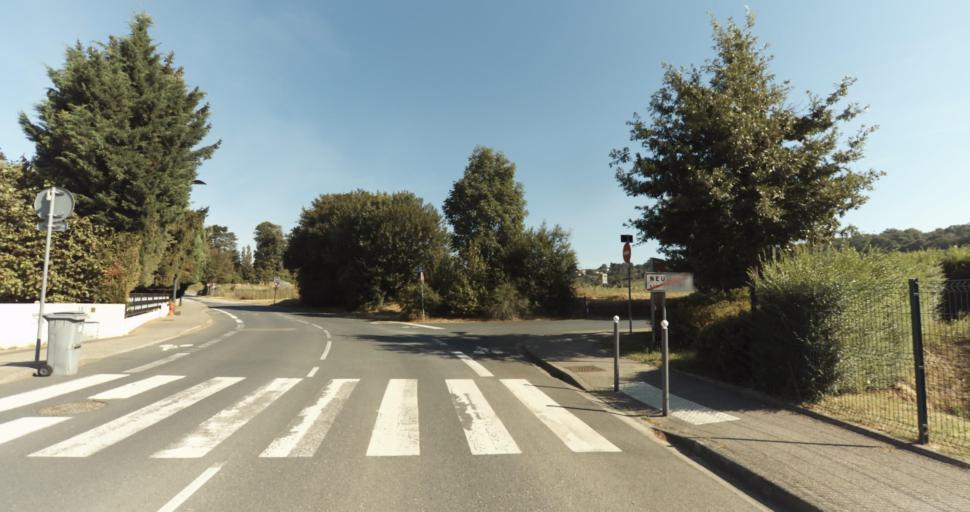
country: FR
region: Rhone-Alpes
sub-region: Departement du Rhone
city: Fleurieu-sur-Saone
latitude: 45.8685
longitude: 4.8477
